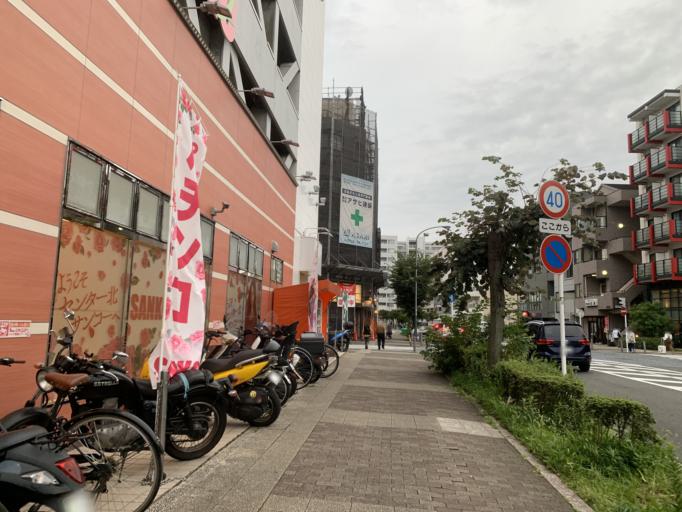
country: JP
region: Tokyo
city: Chofugaoka
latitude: 35.5558
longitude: 139.5807
